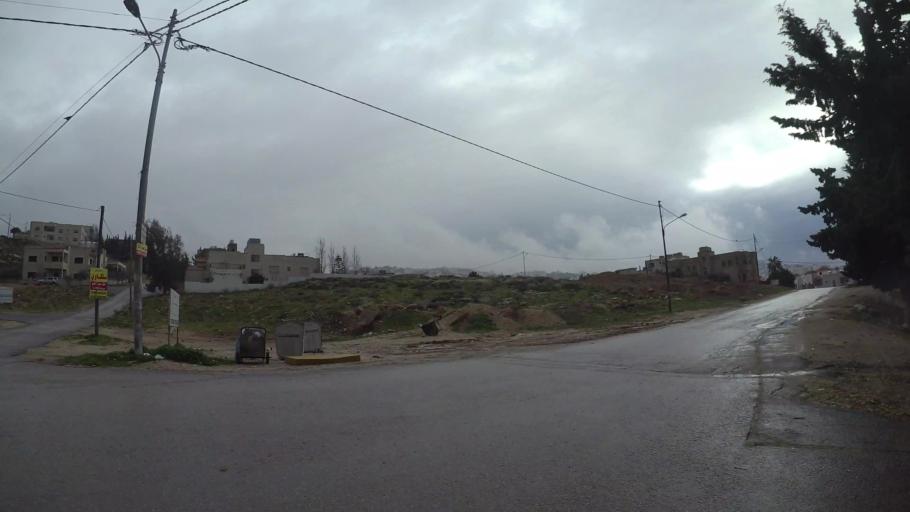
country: JO
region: Amman
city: Al Jubayhah
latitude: 32.0413
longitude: 35.8414
